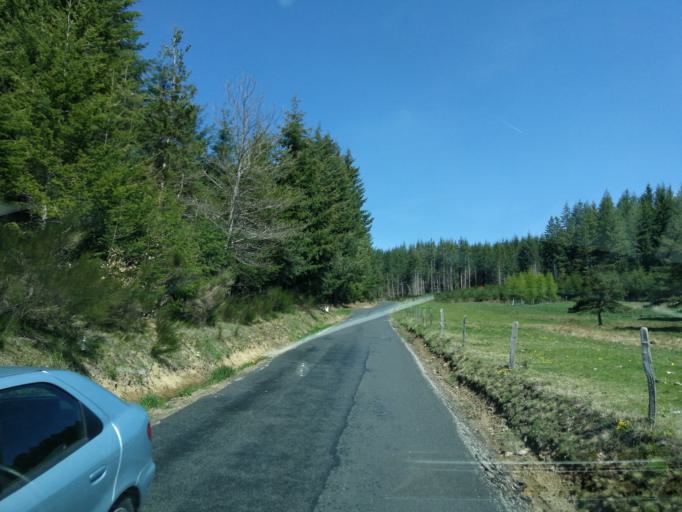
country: FR
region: Rhone-Alpes
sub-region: Departement de l'Ardeche
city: Le Cheylard
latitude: 44.9527
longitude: 4.4179
